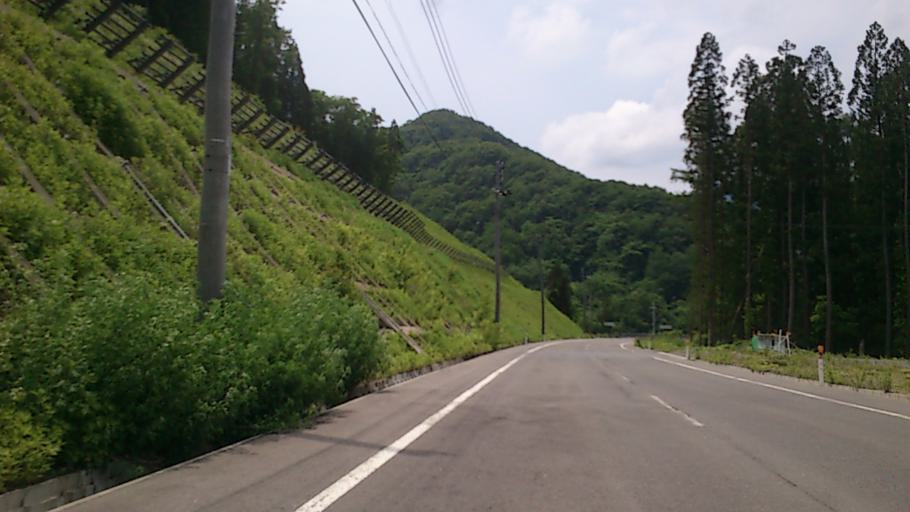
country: JP
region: Aomori
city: Hirosaki
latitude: 40.5188
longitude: 140.2041
